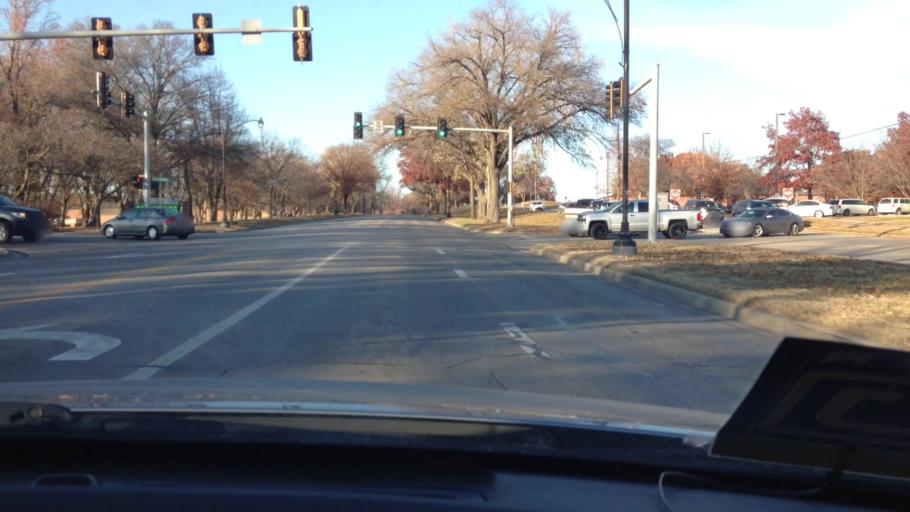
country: US
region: Kansas
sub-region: Leavenworth County
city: Leavenworth
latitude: 39.3378
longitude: -94.9215
